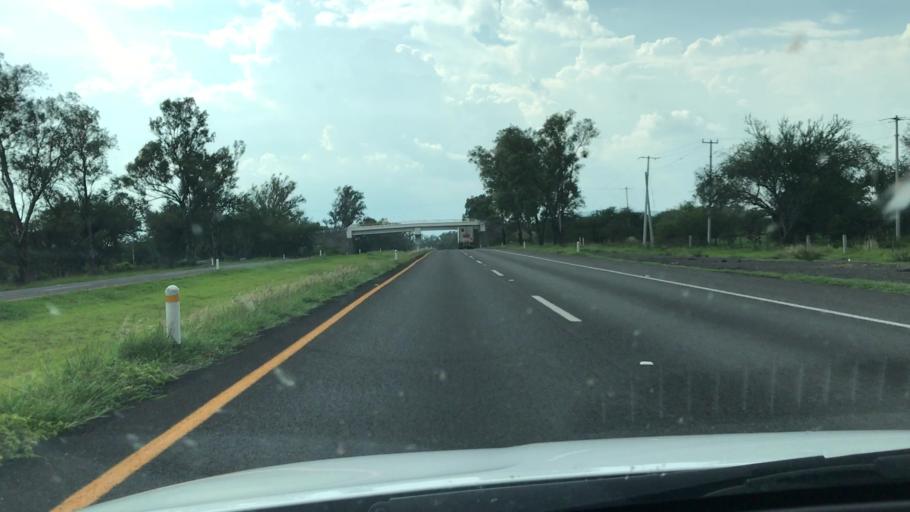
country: MX
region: Jalisco
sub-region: Ocotlan
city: Joconoxtle (La Tuna)
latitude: 20.3670
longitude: -102.6522
